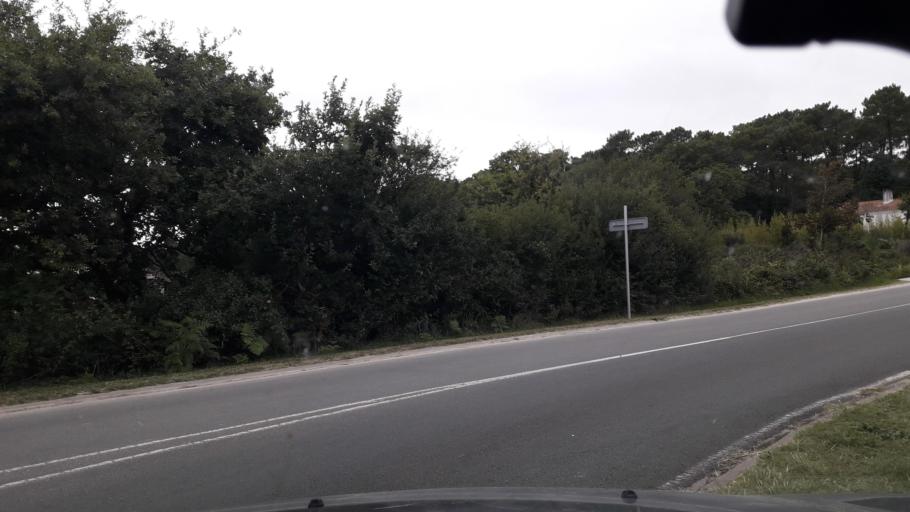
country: FR
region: Poitou-Charentes
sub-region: Departement de la Charente-Maritime
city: Les Mathes
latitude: 45.7042
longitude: -1.1669
